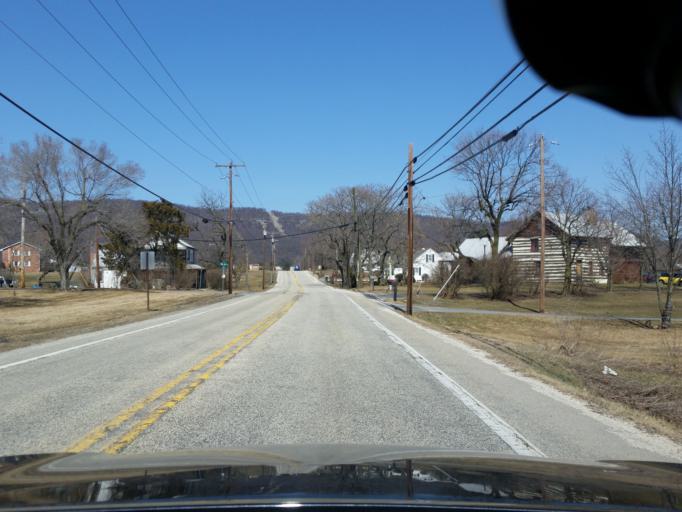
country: US
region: Pennsylvania
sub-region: Cumberland County
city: Schlusser
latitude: 40.2629
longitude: -77.1695
